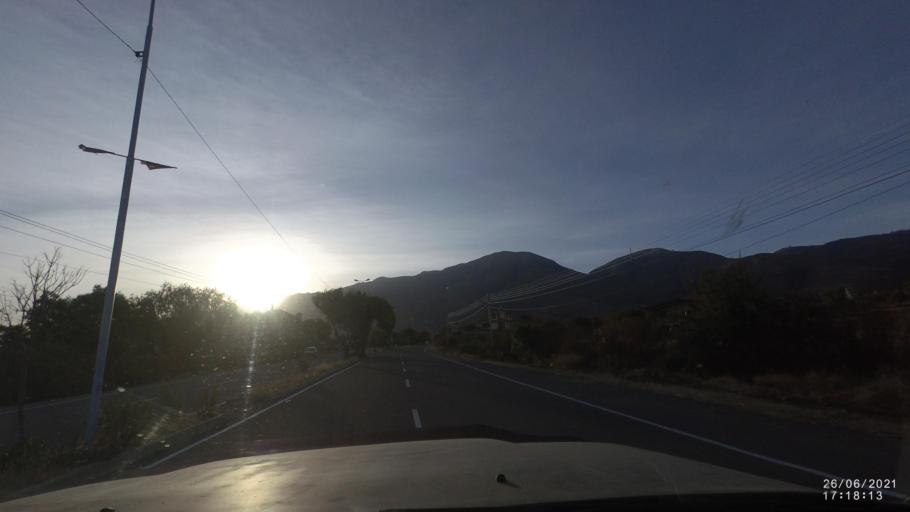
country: BO
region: Cochabamba
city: Cliza
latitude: -17.5389
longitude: -65.9592
